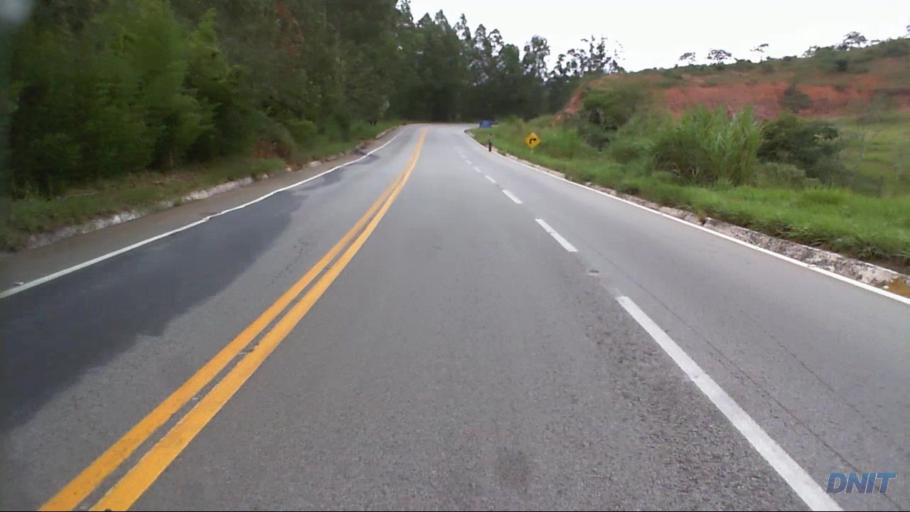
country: BR
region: Minas Gerais
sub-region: Nova Era
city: Nova Era
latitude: -19.7834
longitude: -43.0444
